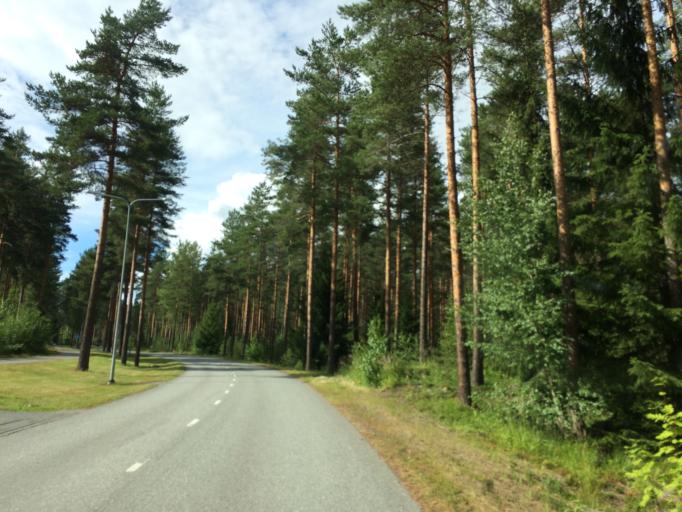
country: FI
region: Haeme
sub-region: Haemeenlinna
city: Turenki
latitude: 60.9362
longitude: 24.6510
